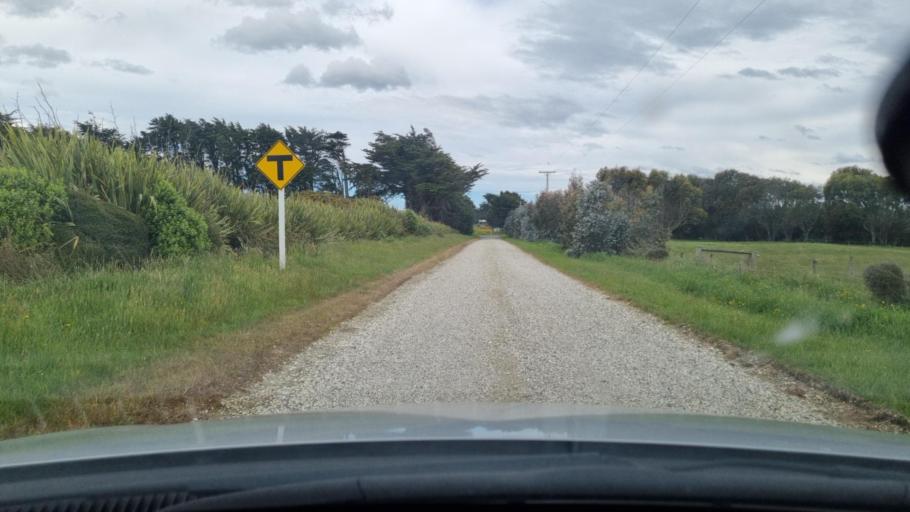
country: NZ
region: Southland
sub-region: Invercargill City
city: Invercargill
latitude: -46.4072
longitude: 168.2598
